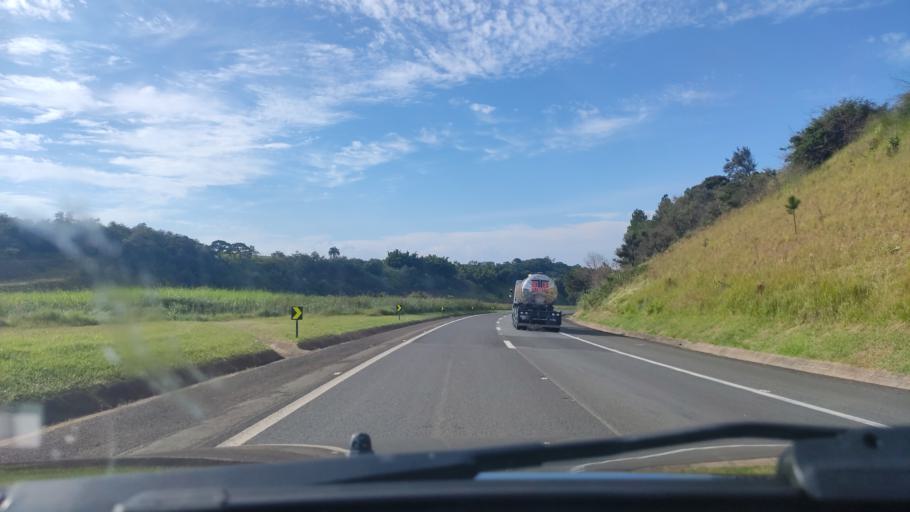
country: BR
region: Sao Paulo
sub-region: Itatinga
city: Itatinga
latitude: -23.0882
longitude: -48.5085
